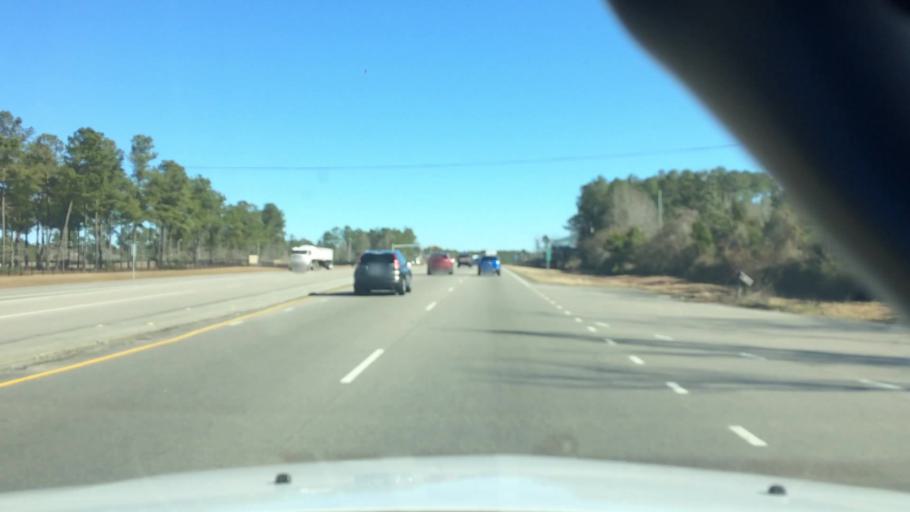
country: US
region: North Carolina
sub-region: Brunswick County
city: Bolivia
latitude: 34.0292
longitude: -78.2588
